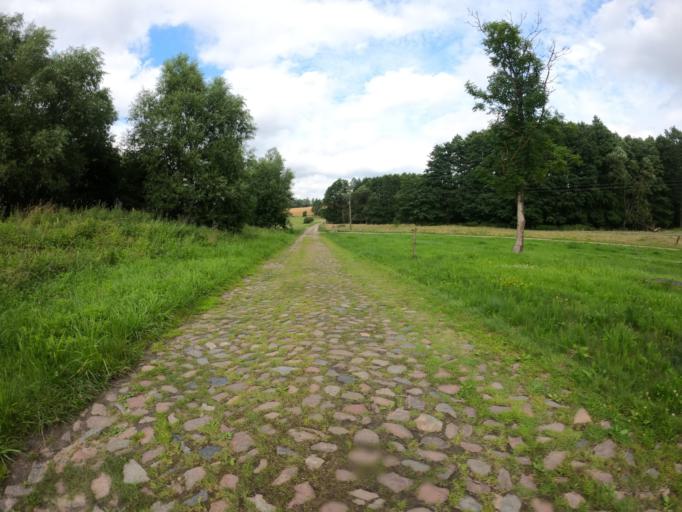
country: PL
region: West Pomeranian Voivodeship
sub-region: Powiat szczecinecki
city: Grzmiaca
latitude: 53.7983
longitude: 16.4728
